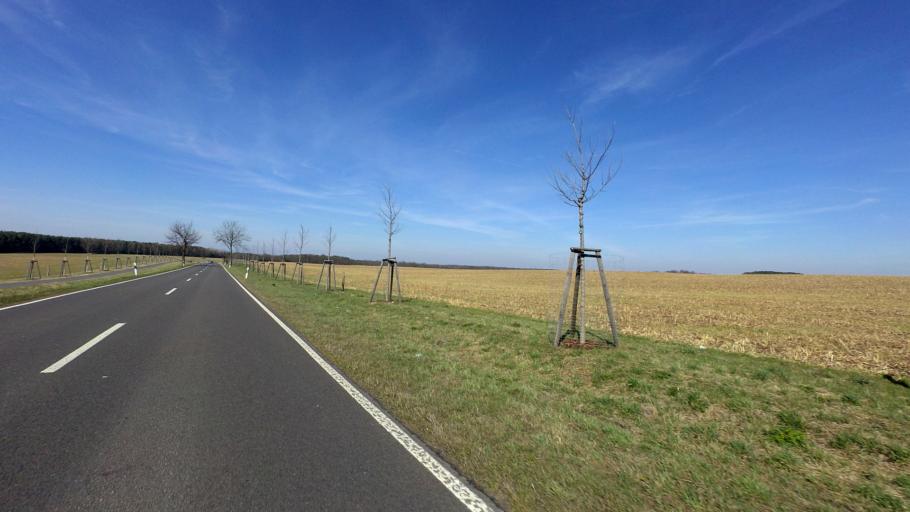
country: DE
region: Brandenburg
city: Furstenwalde
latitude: 52.3902
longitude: 14.0490
